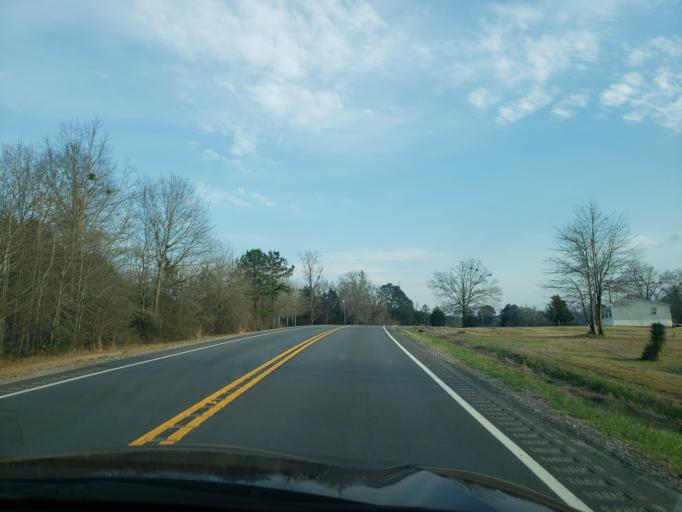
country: US
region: Alabama
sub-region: Hale County
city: Moundville
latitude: 32.8887
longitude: -87.6104
